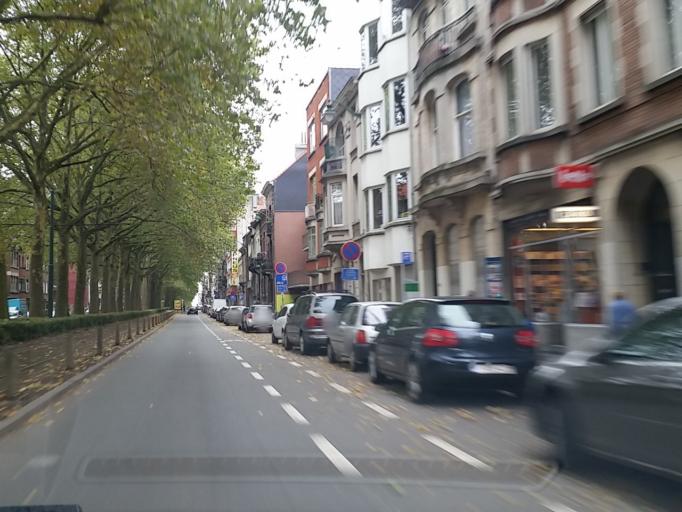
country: BE
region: Flanders
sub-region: Provincie Vlaams-Brabant
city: Drogenbos
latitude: 50.8156
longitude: 4.3252
